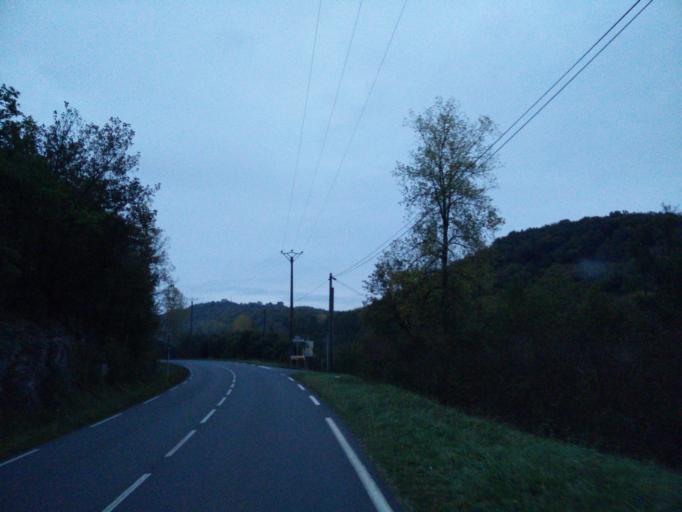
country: FR
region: Aquitaine
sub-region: Departement de la Dordogne
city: Saint-Cyprien
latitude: 44.9255
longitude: 1.0814
